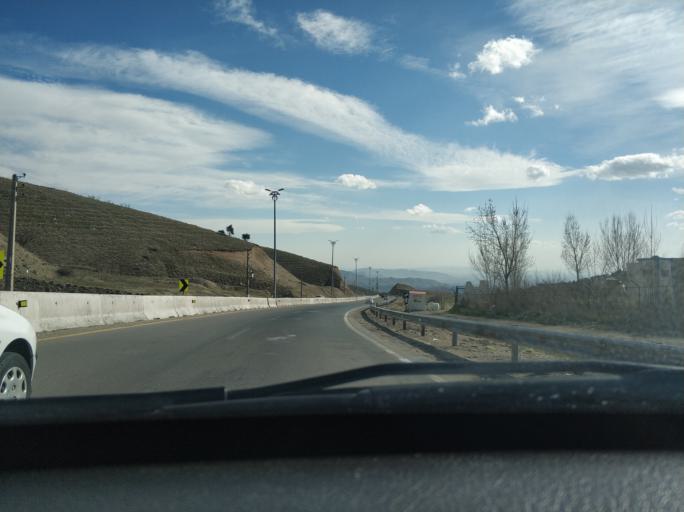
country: IR
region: Tehran
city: Tajrish
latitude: 35.8028
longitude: 51.5732
